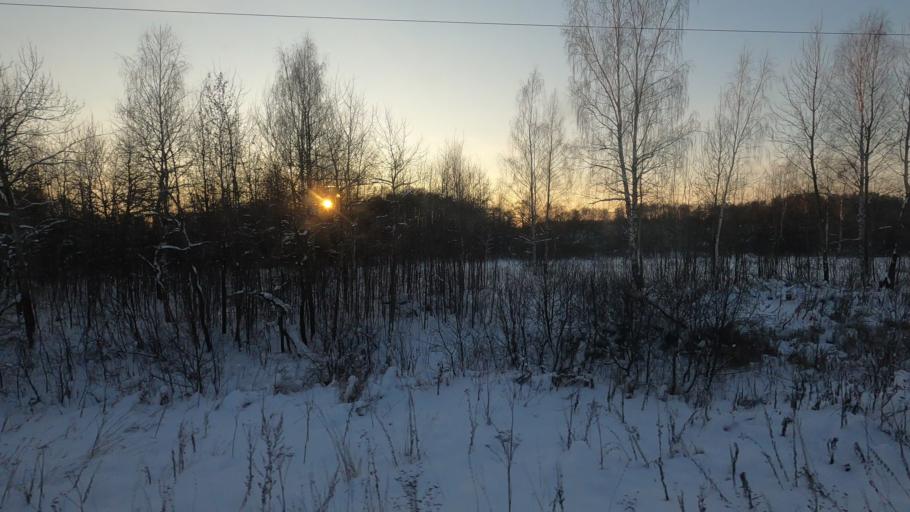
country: RU
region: Moskovskaya
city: Dmitrov
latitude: 56.3884
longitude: 37.5097
